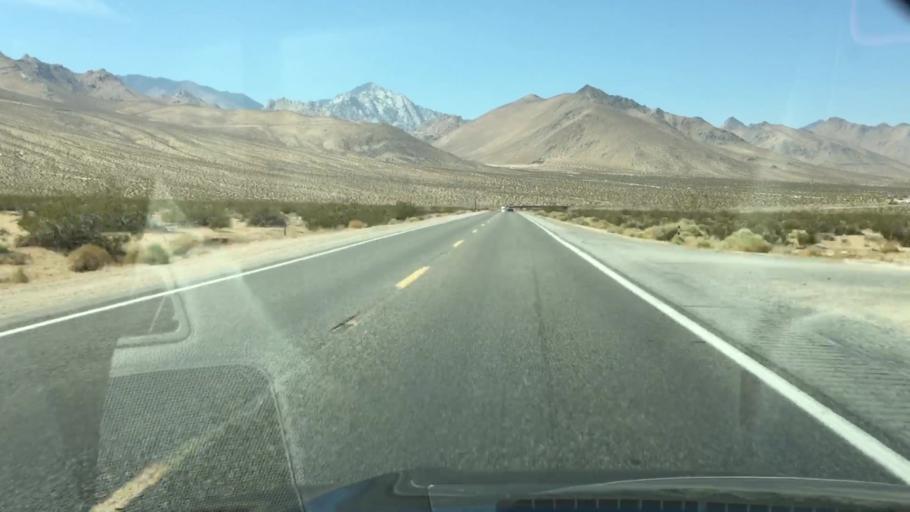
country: US
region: California
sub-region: Kern County
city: Inyokern
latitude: 35.6892
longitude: -117.8575
